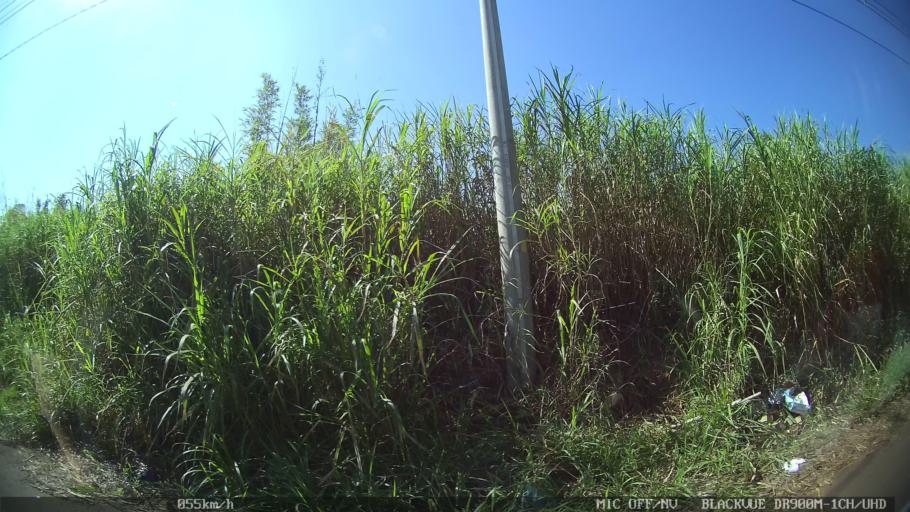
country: BR
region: Sao Paulo
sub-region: Valinhos
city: Valinhos
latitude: -23.0148
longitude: -47.0911
